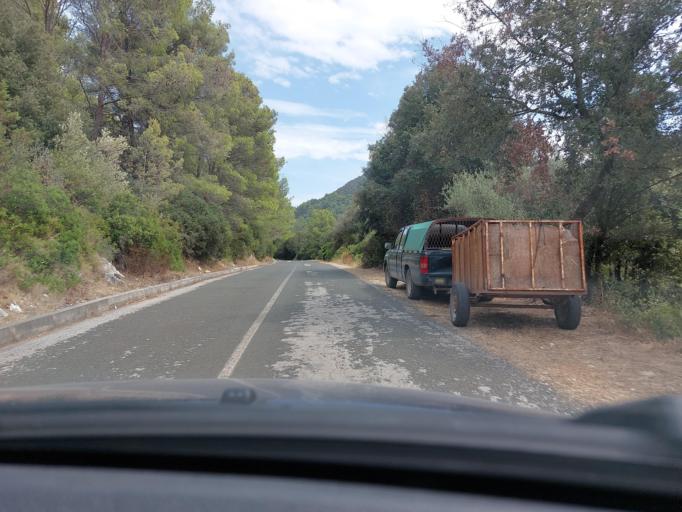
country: HR
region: Dubrovacko-Neretvanska
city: Smokvica
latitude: 42.7614
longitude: 16.8987
